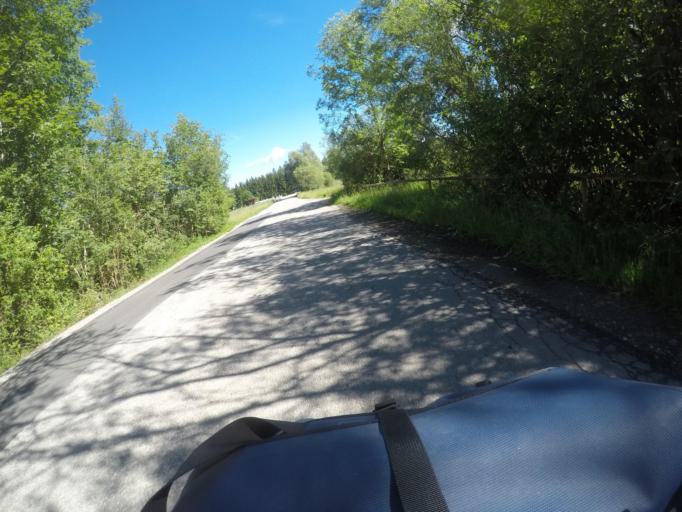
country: AT
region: Tyrol
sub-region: Politischer Bezirk Reutte
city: Vils
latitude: 47.5722
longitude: 10.6551
